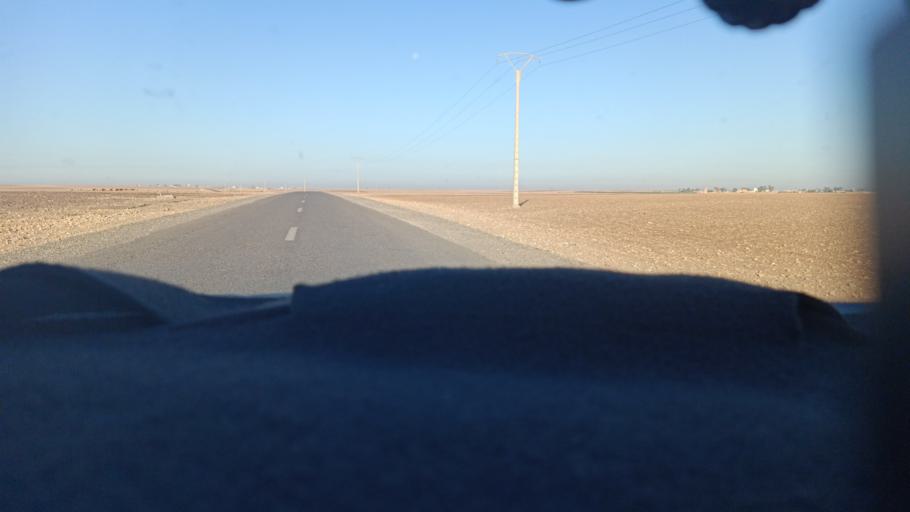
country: MA
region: Doukkala-Abda
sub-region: Safi
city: Youssoufia
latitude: 32.3720
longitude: -8.6402
